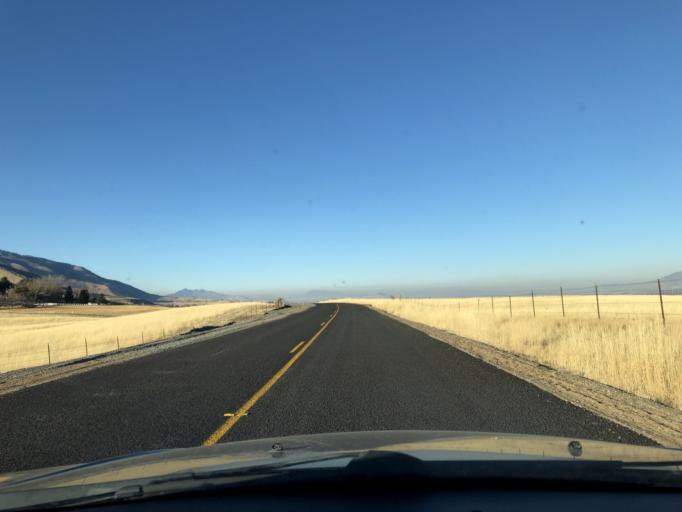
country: US
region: Utah
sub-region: Cache County
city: Wellsville
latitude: 41.5917
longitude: -111.9268
